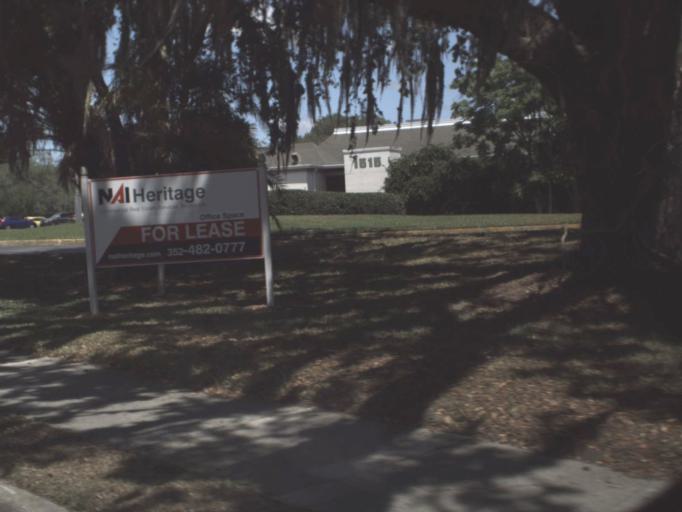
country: US
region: Florida
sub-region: Marion County
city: Ocala
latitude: 29.1870
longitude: -82.1177
